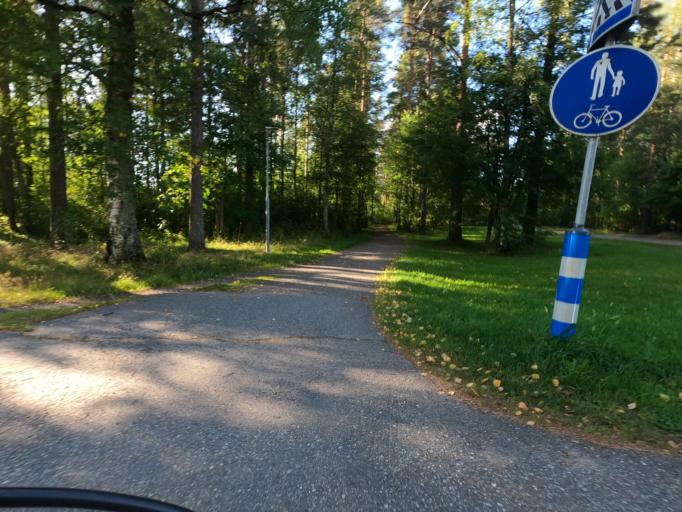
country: FI
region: North Karelia
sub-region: Joensuu
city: Joensuu
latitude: 62.6113
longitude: 29.7467
